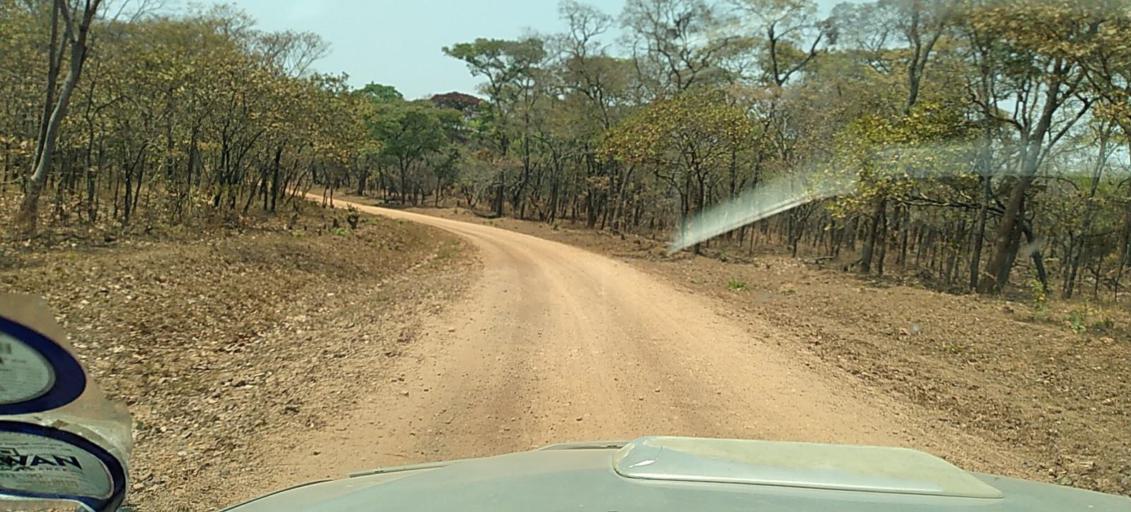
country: ZM
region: North-Western
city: Kasempa
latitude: -13.5561
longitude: 26.0699
